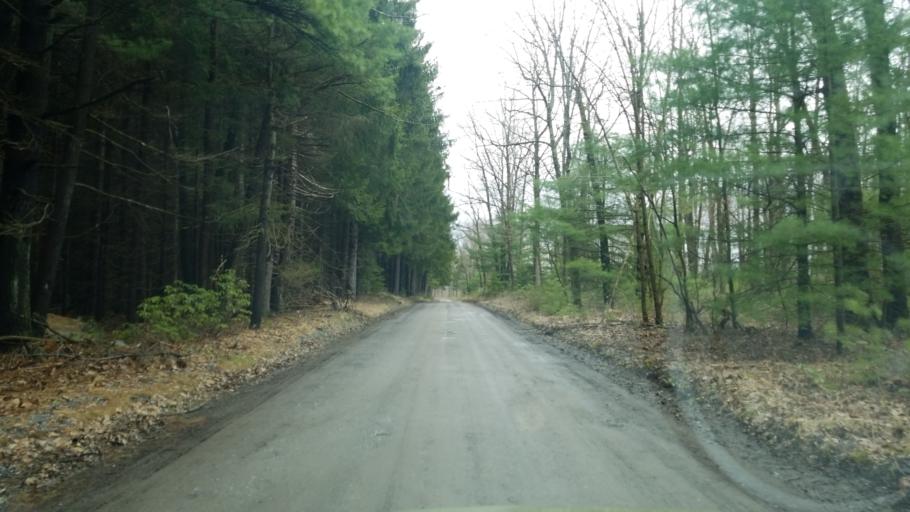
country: US
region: Pennsylvania
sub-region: Clearfield County
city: Shiloh
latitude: 41.1684
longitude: -78.2723
